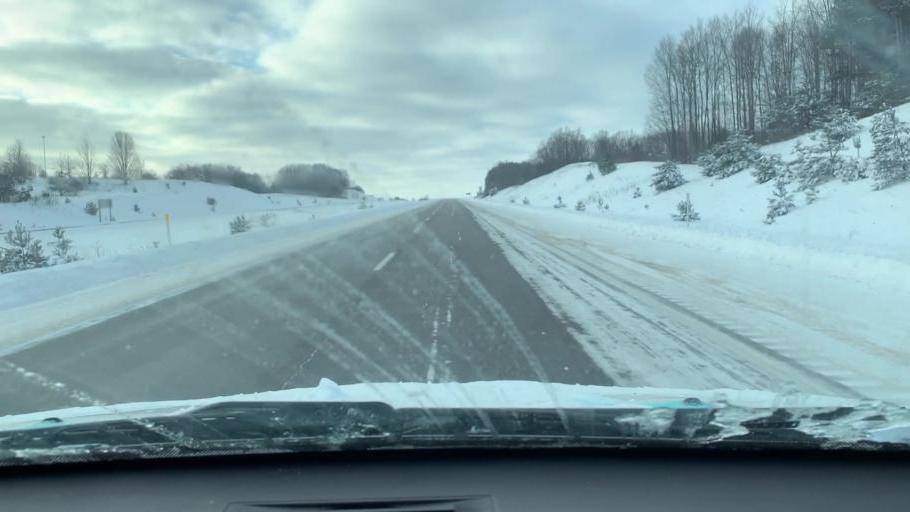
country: US
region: Michigan
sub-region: Wexford County
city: Manton
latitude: 44.3977
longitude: -85.3822
